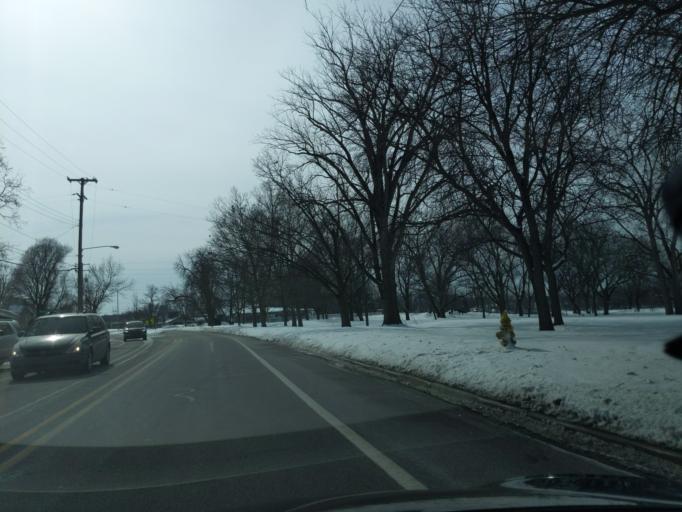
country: US
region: Michigan
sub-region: Kent County
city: Grand Rapids
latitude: 43.0007
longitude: -85.6702
